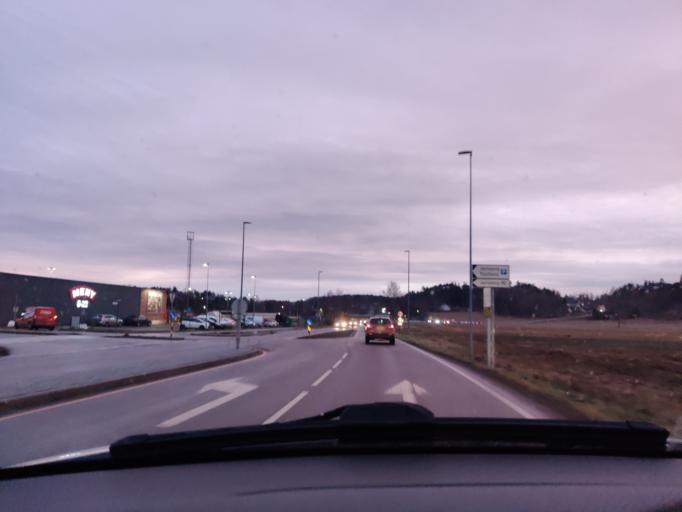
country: NO
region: Vestfold
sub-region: Tonsberg
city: Sem
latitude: 59.2808
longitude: 10.3639
